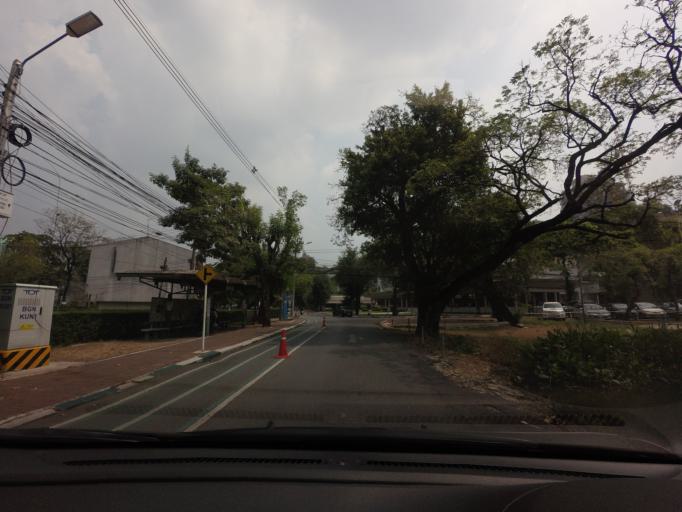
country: TH
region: Bangkok
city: Chatuchak
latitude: 13.8472
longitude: 100.5679
